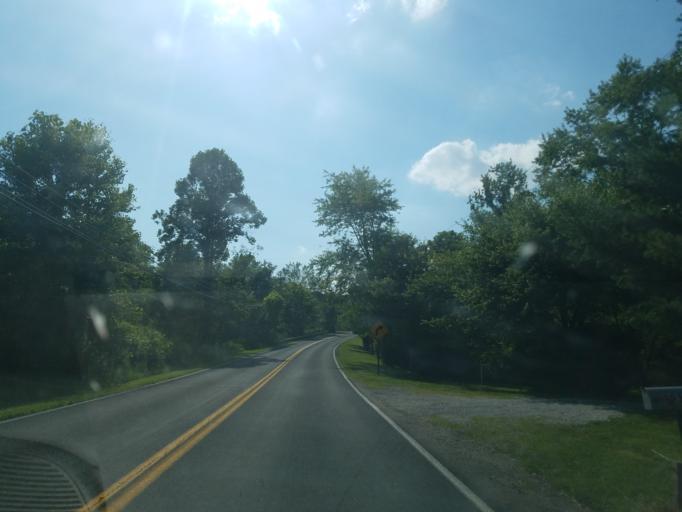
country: US
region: Ohio
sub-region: Summit County
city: Mogadore
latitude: 41.0437
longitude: -81.3559
